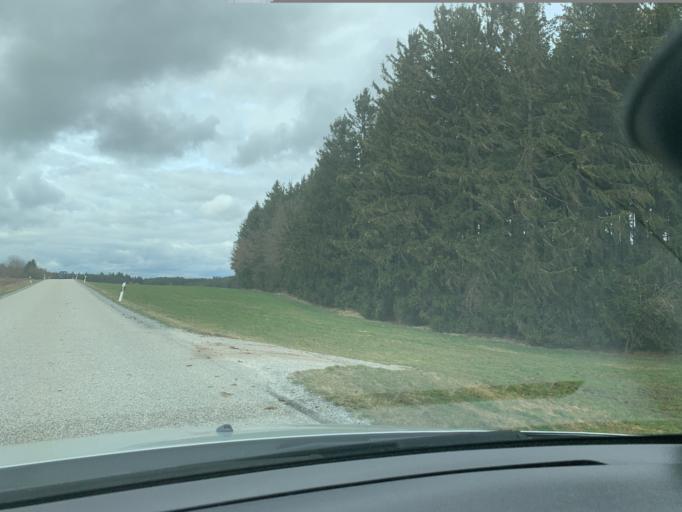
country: DE
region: Bavaria
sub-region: Lower Bavaria
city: Vilsbiburg
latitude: 48.4631
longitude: 12.3318
